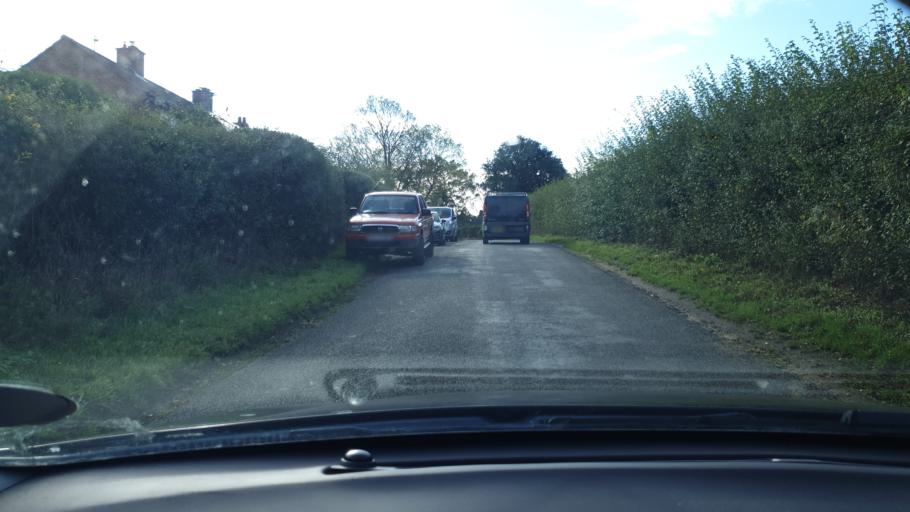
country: GB
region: England
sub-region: Essex
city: Alresford
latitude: 51.8628
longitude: 1.0184
